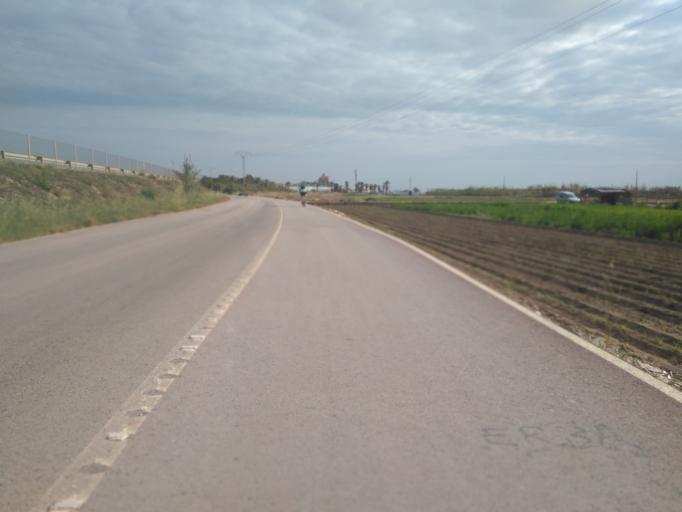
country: ES
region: Valencia
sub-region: Provincia de Valencia
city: Alboraya
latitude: 39.4982
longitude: -0.3256
